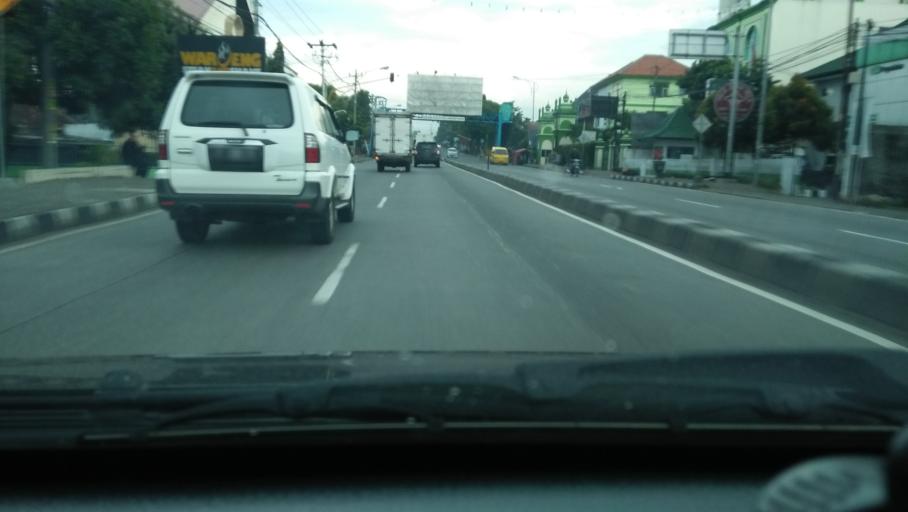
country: ID
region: Central Java
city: Ungaran
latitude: -7.1334
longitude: 110.4039
